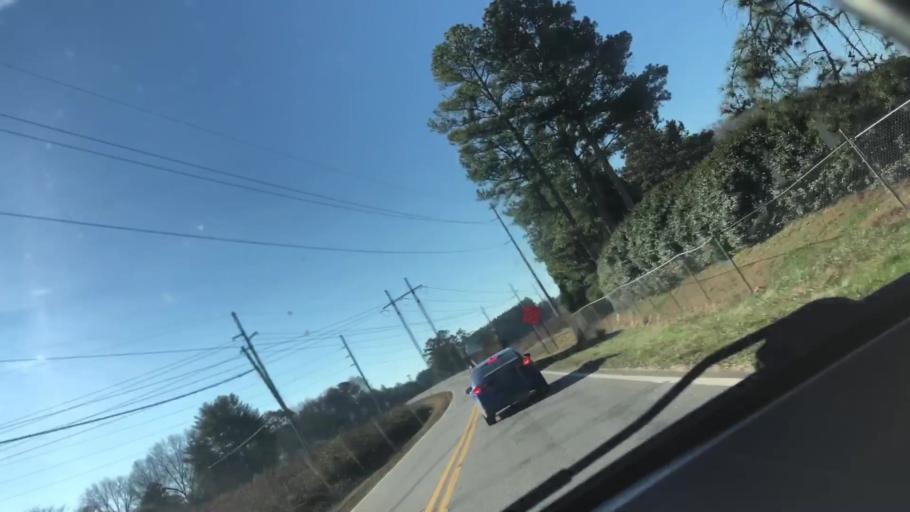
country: US
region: Georgia
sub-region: Bartow County
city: Cartersville
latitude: 34.2146
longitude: -84.8021
